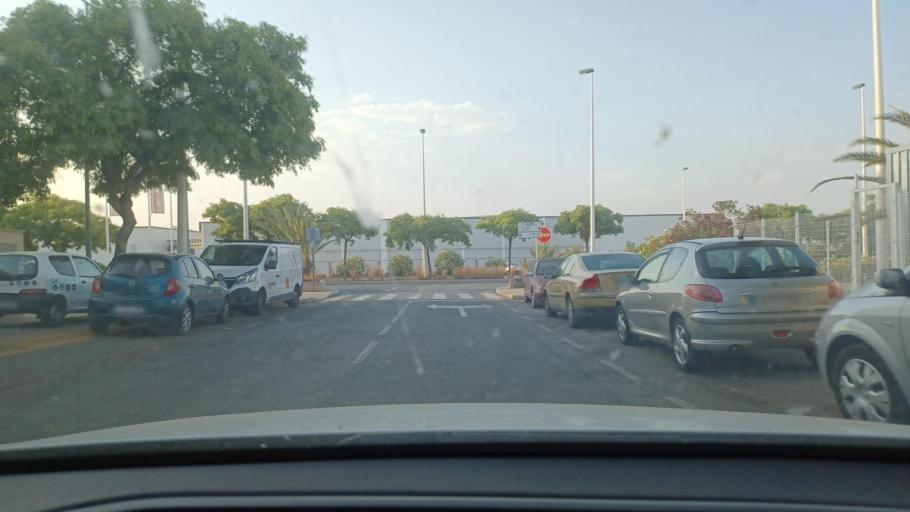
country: ES
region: Valencia
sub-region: Provincia de Alicante
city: Elche
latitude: 38.2929
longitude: -0.6186
